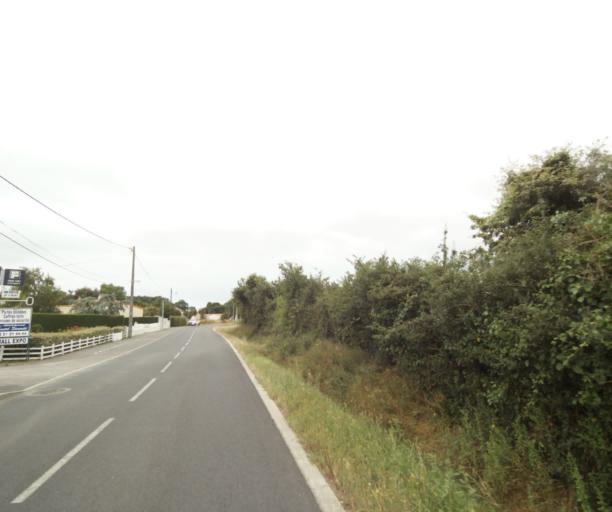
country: FR
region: Pays de la Loire
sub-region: Departement de la Vendee
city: Chateau-d'Olonne
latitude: 46.5105
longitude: -1.7393
